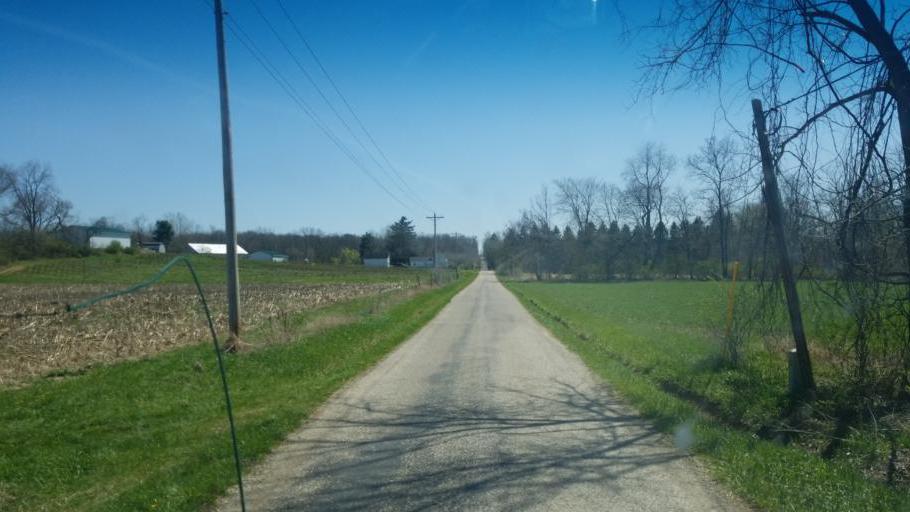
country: US
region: Ohio
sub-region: Ashland County
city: Ashland
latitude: 40.8340
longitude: -82.3877
